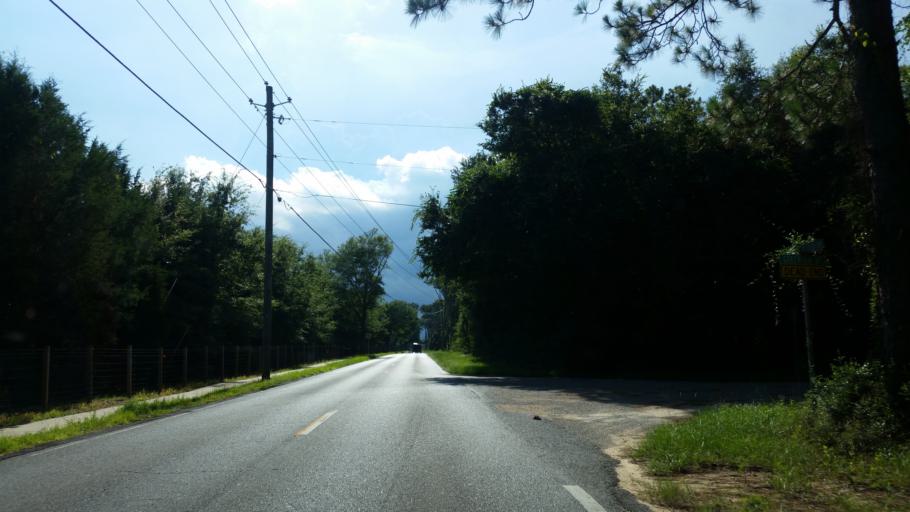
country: US
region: Florida
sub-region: Santa Rosa County
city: Pace
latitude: 30.6323
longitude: -87.1339
